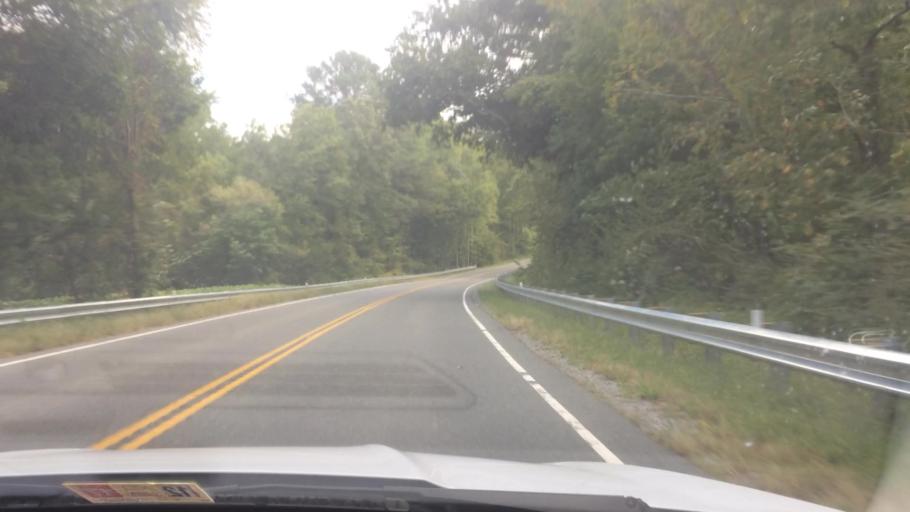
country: US
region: Virginia
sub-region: Northumberland County
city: Heathsville
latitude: 37.8504
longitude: -76.5846
